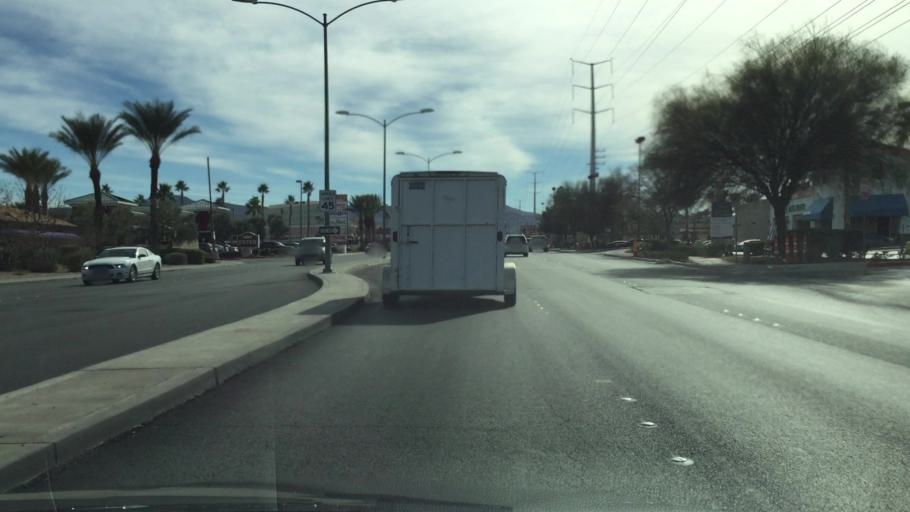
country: US
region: Nevada
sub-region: Clark County
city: Whitney
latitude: 36.0630
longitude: -115.0462
